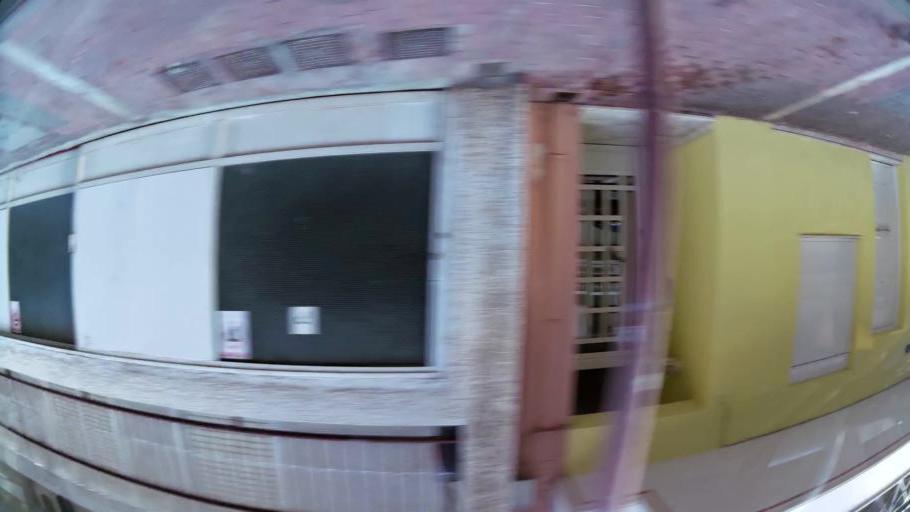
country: GR
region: Attica
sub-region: Nomarchia Athinas
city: Dhafni
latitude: 37.9557
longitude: 23.7377
